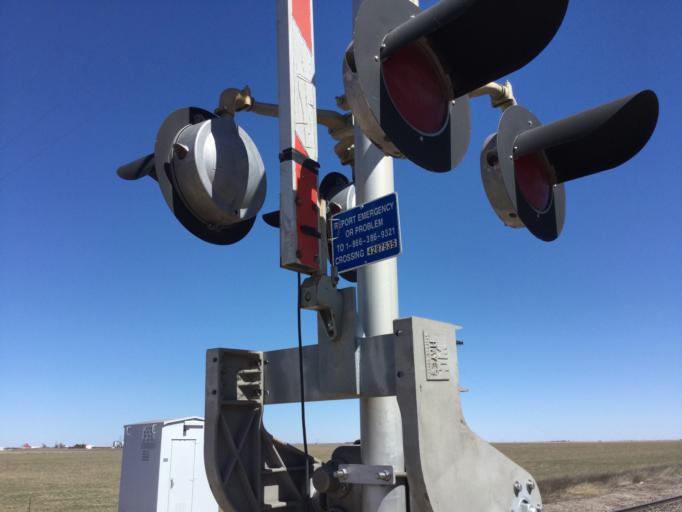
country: US
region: Kansas
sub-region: Wichita County
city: Leoti
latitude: 38.4857
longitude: -101.3125
